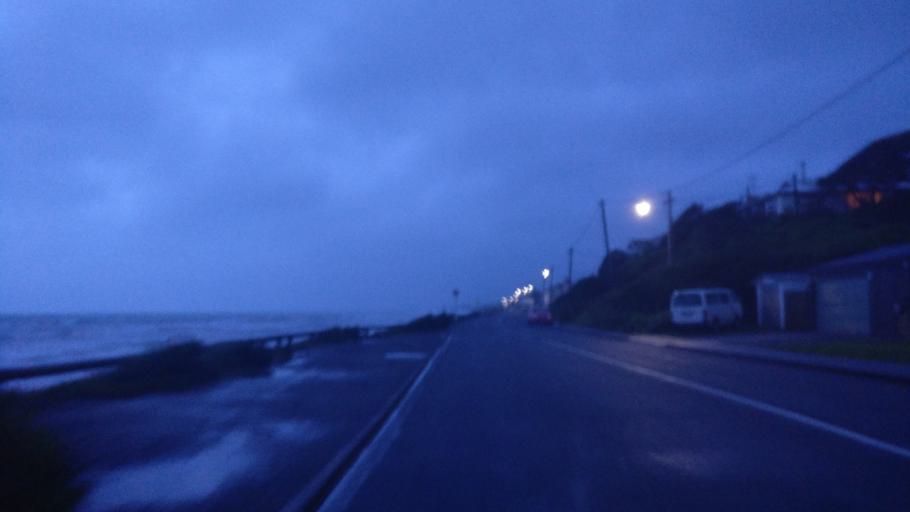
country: NZ
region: Wellington
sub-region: Kapiti Coast District
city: Paraparaumu
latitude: -40.9820
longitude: 174.9538
